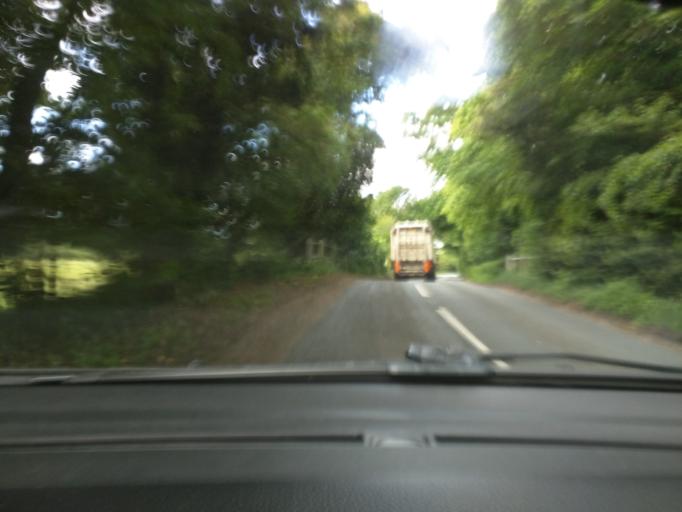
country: GB
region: England
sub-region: Suffolk
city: Saxmundham
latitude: 52.2286
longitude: 1.4459
